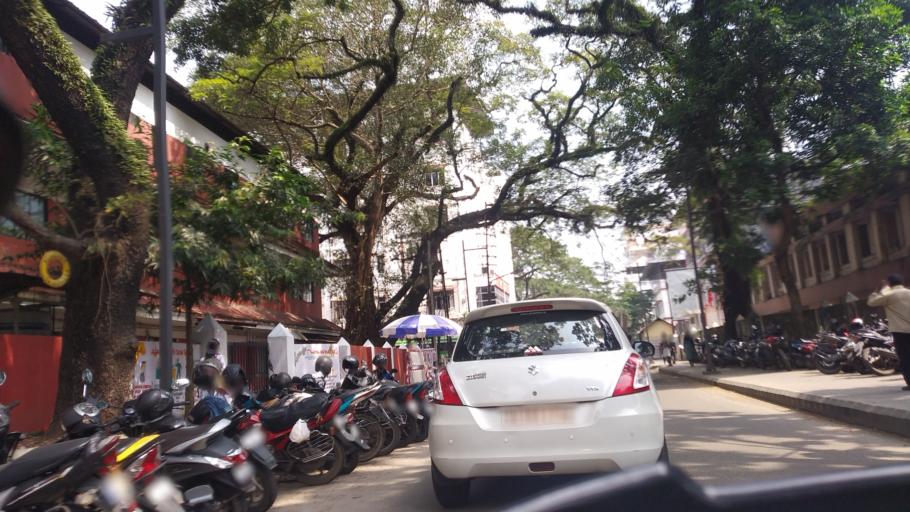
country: IN
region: Kerala
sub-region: Ernakulam
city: Cochin
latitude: 9.9716
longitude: 76.2815
